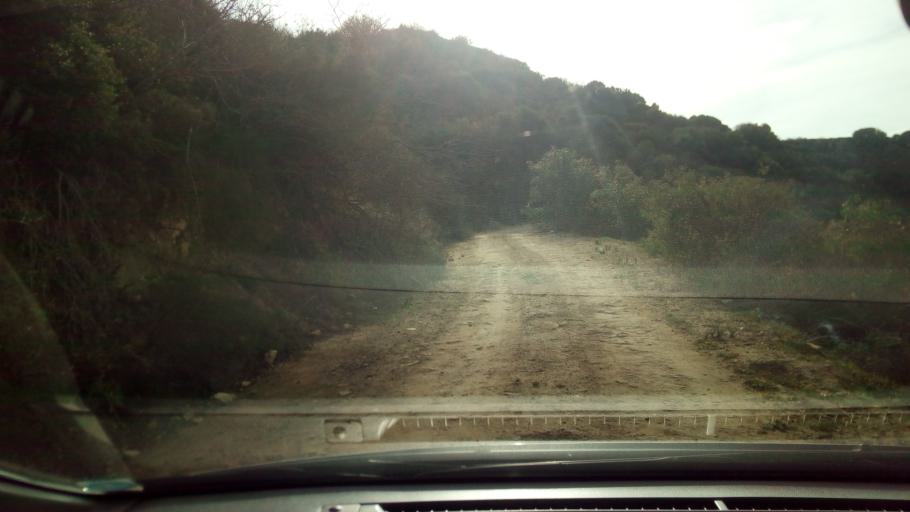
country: CY
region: Pafos
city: Mesogi
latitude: 34.7984
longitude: 32.5470
